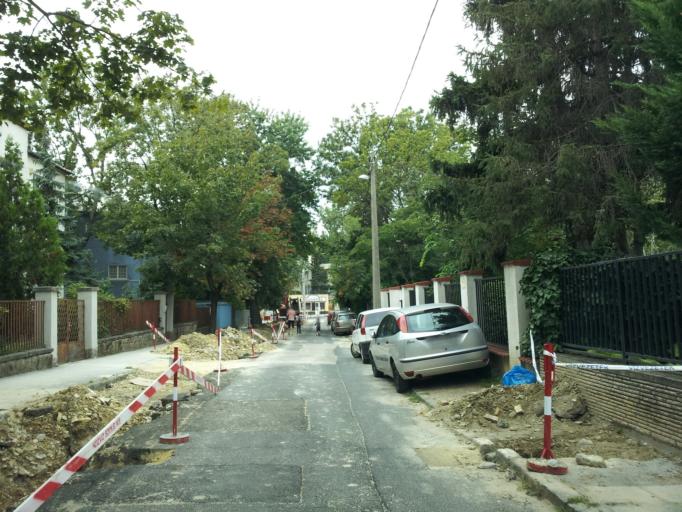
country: HU
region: Budapest
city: Budapest II. keruelet
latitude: 47.5215
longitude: 19.0223
